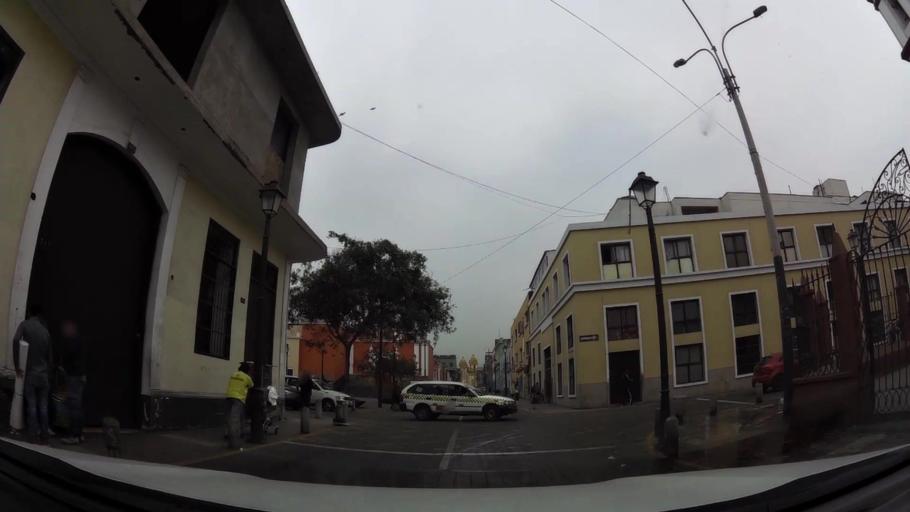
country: PE
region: Lima
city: Lima
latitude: -12.0474
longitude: -77.0228
